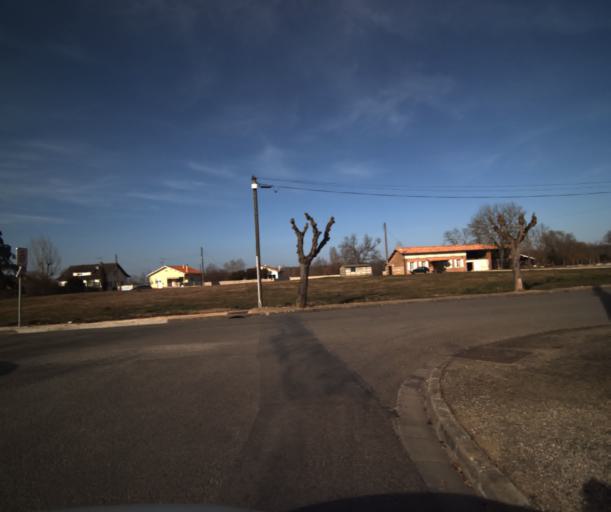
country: FR
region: Midi-Pyrenees
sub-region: Departement du Tarn-et-Garonne
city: Labastide-Saint-Pierre
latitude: 43.9185
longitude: 1.3701
